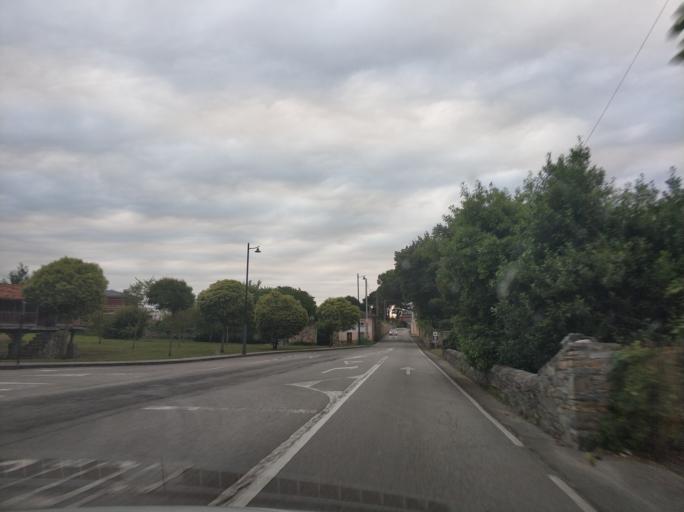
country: ES
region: Asturias
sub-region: Province of Asturias
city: Navia
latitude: 43.5426
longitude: -6.5243
